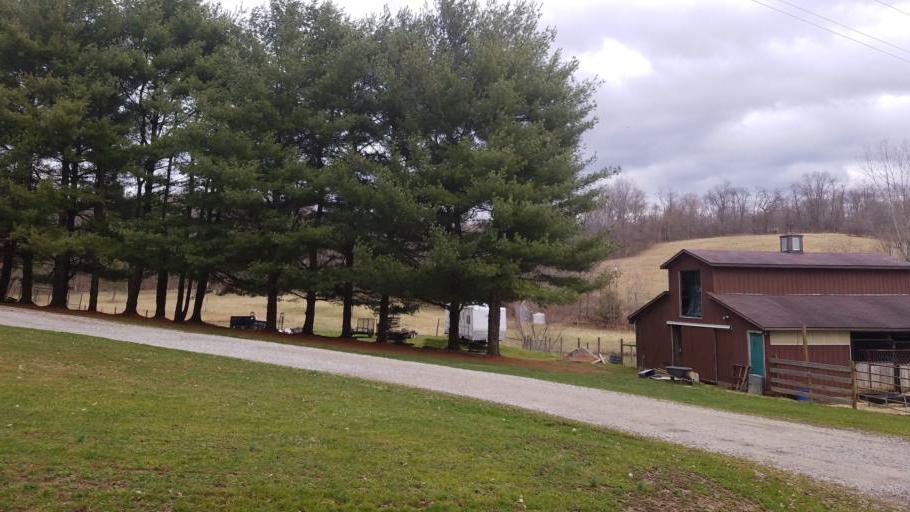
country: US
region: Ohio
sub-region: Muskingum County
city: Frazeysburg
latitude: 40.1385
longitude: -82.2369
